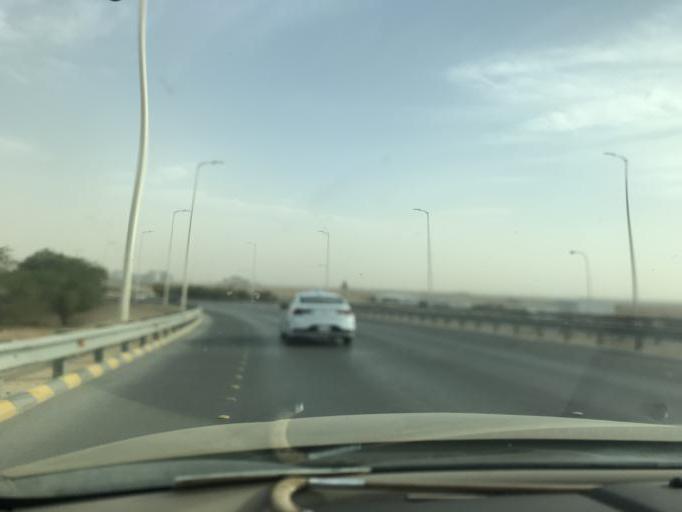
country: SA
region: Ar Riyad
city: Riyadh
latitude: 24.9441
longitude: 46.7062
